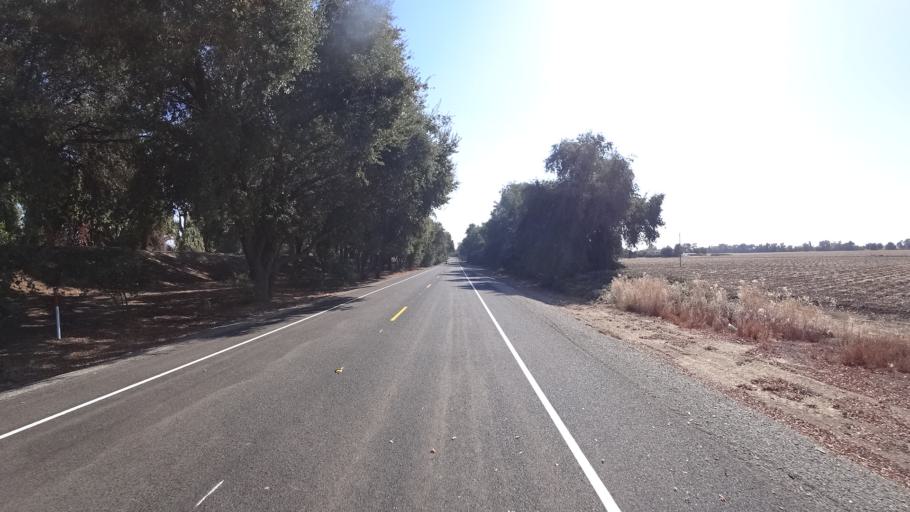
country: US
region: California
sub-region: Yolo County
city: West Sacramento
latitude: 38.6651
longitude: -121.6184
